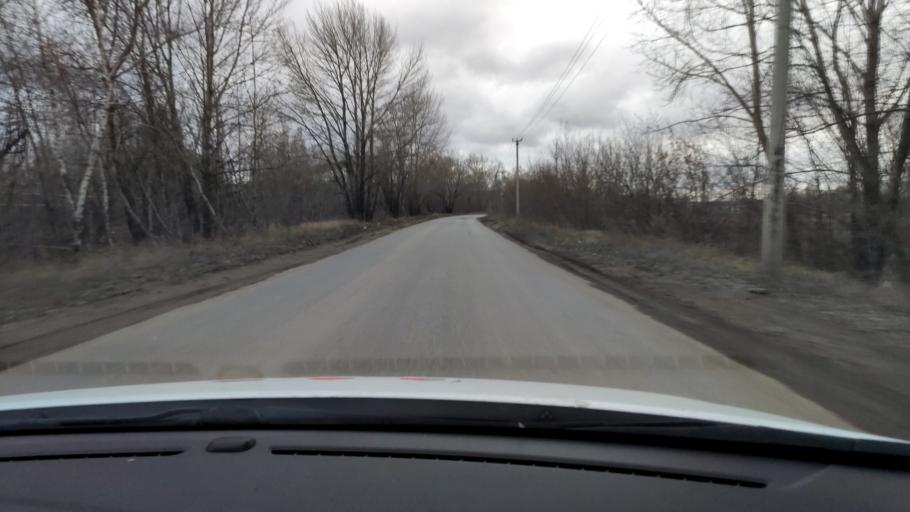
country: RU
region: Tatarstan
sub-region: Gorod Kazan'
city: Kazan
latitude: 55.7240
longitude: 49.0953
